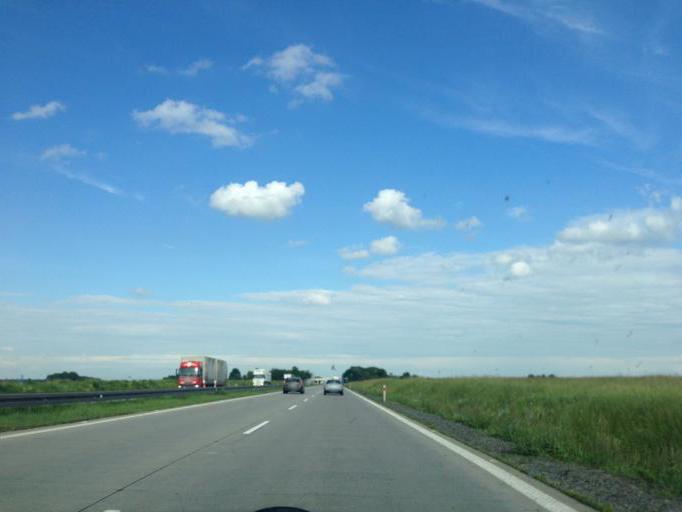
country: PL
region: Lower Silesian Voivodeship
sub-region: Powiat wroclawski
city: Gniechowice
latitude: 51.0350
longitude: 16.8178
